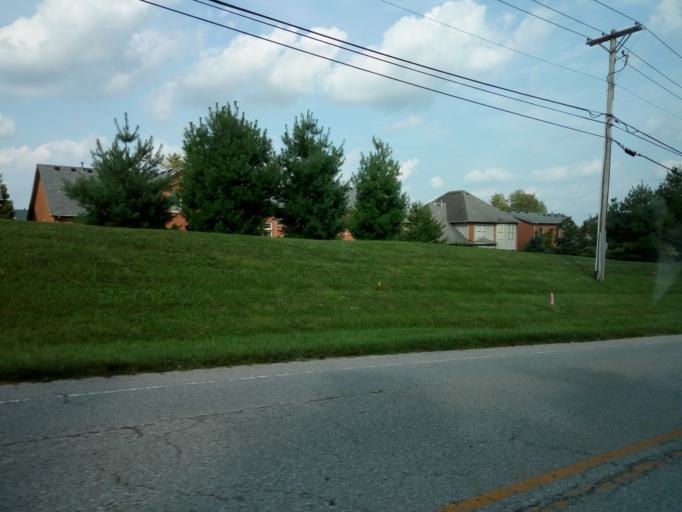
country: US
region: Kentucky
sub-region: Oldham County
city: Pewee Valley
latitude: 38.2720
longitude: -85.4854
